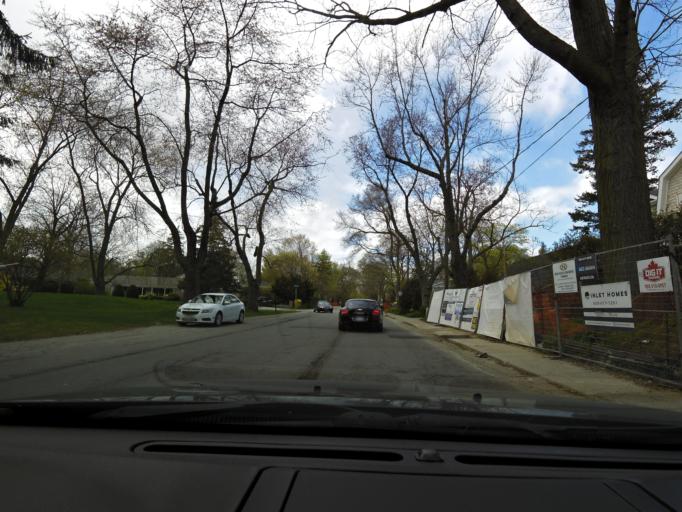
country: CA
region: Ontario
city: Oakville
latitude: 43.4505
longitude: -79.6650
